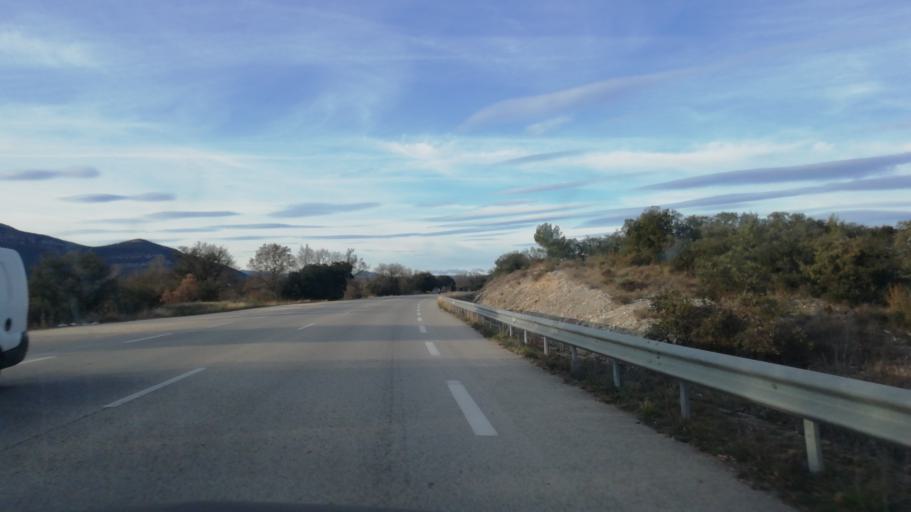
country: FR
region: Languedoc-Roussillon
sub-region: Departement du Gard
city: Quissac
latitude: 43.8954
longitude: 4.0088
